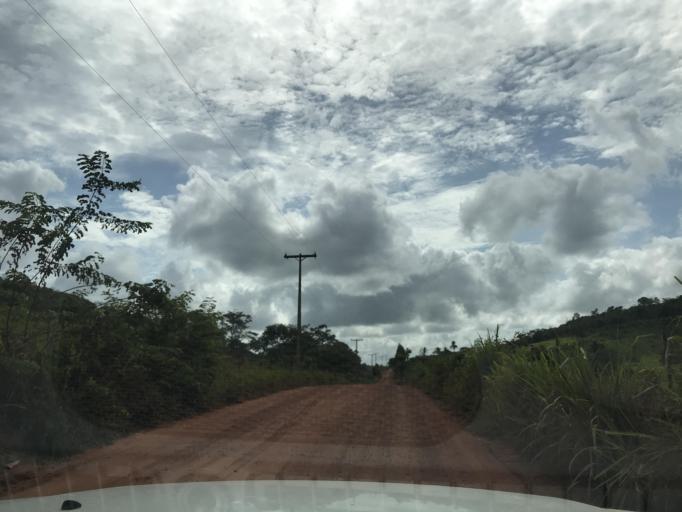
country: BR
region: Bahia
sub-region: Entre Rios
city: Entre Rios
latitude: -12.1655
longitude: -38.1594
